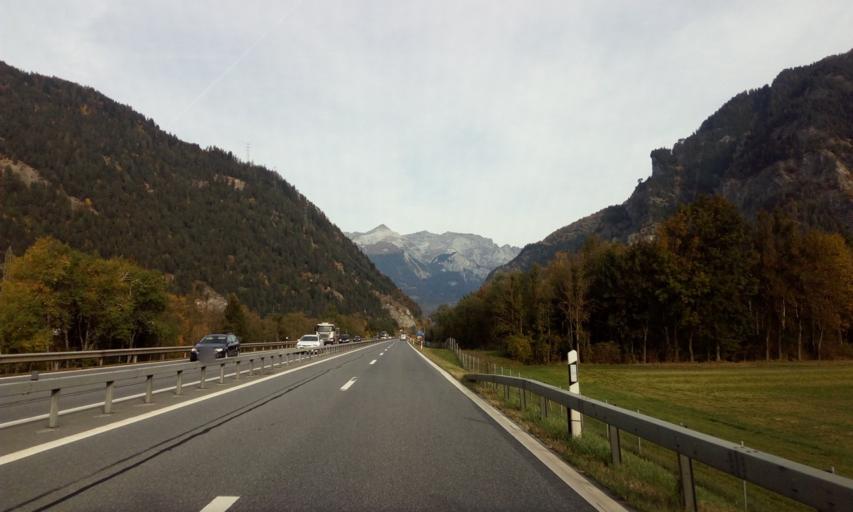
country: CH
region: Grisons
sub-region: Hinterrhein District
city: Cazis
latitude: 46.7570
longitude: 9.4257
